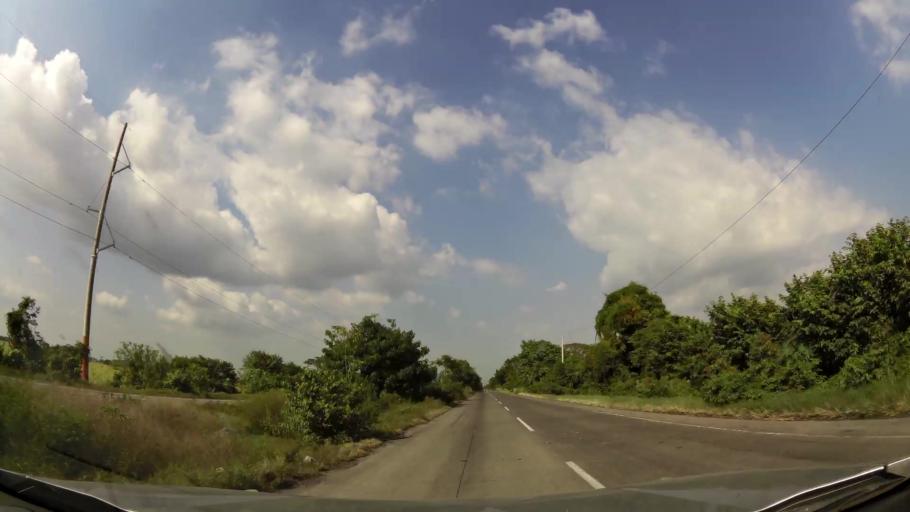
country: GT
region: Escuintla
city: Puerto San Jose
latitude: 14.0243
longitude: -90.7822
